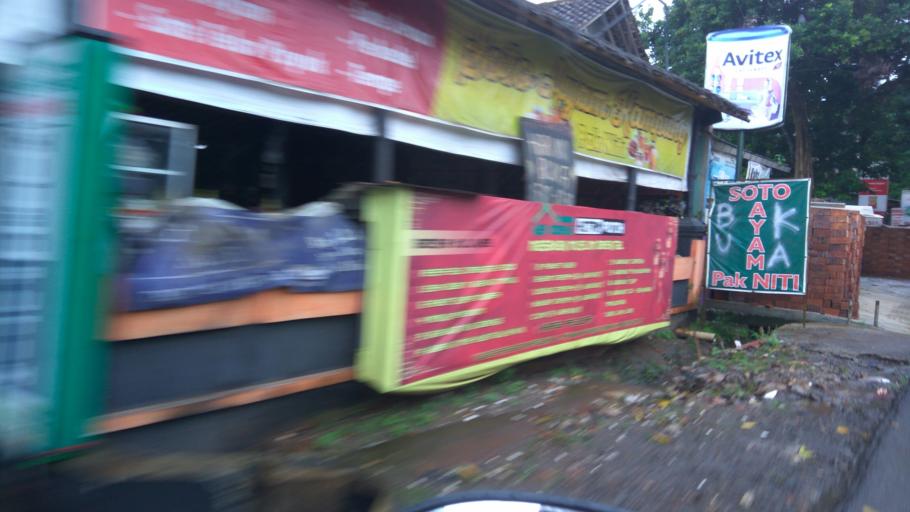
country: ID
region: Central Java
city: Semarang
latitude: -7.0576
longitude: 110.3968
